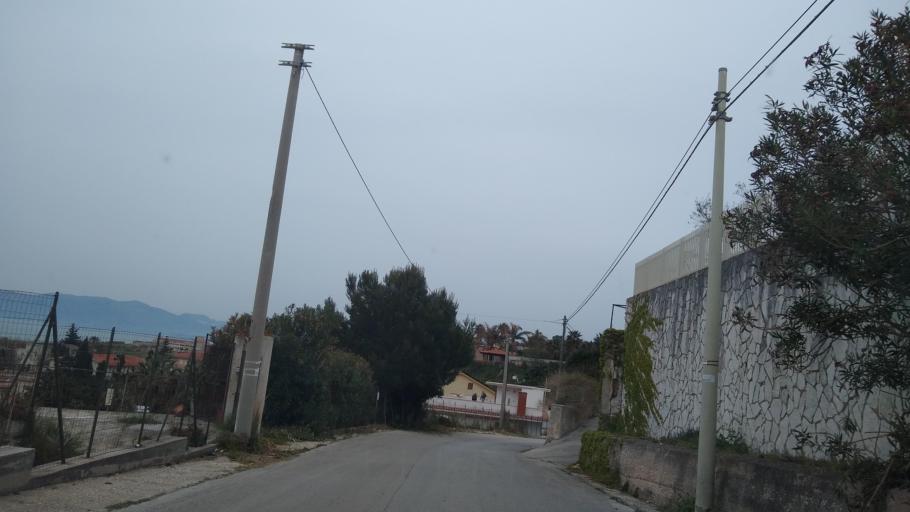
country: IT
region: Sicily
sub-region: Trapani
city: Castellammare del Golfo
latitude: 38.0218
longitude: 12.9006
